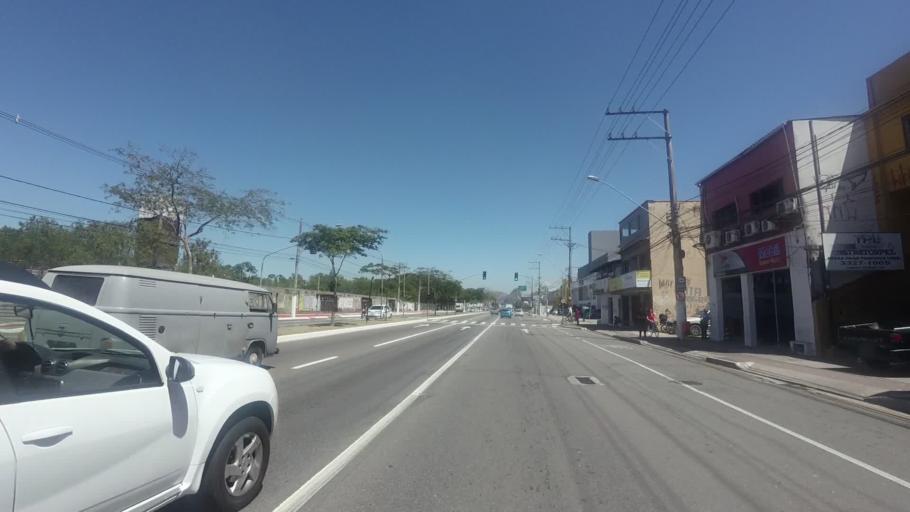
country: BR
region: Espirito Santo
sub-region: Vila Velha
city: Vila Velha
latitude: -20.2626
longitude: -40.2947
